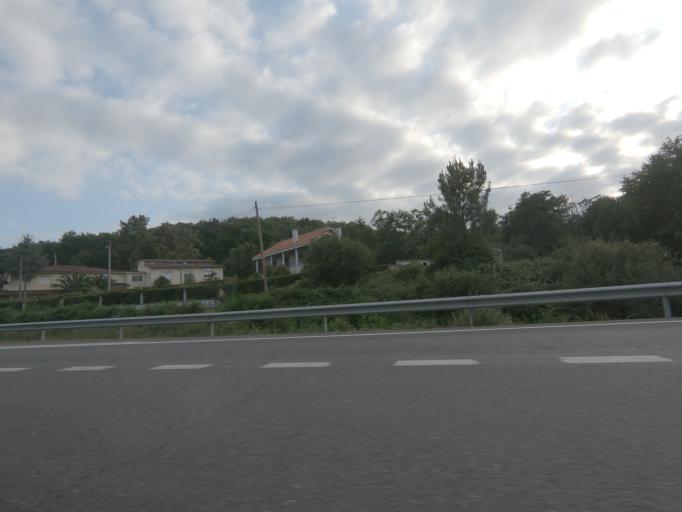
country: ES
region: Galicia
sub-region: Provincia de Ourense
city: Taboadela
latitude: 42.2366
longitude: -7.8458
